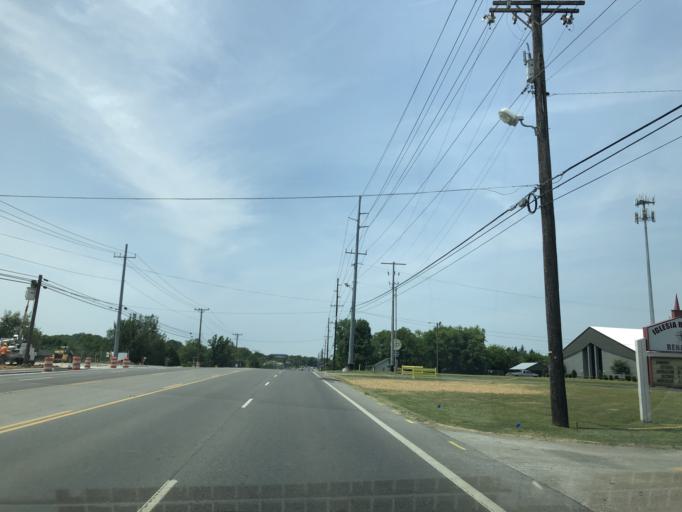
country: US
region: Tennessee
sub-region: Rutherford County
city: La Vergne
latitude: 36.0471
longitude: -86.6113
